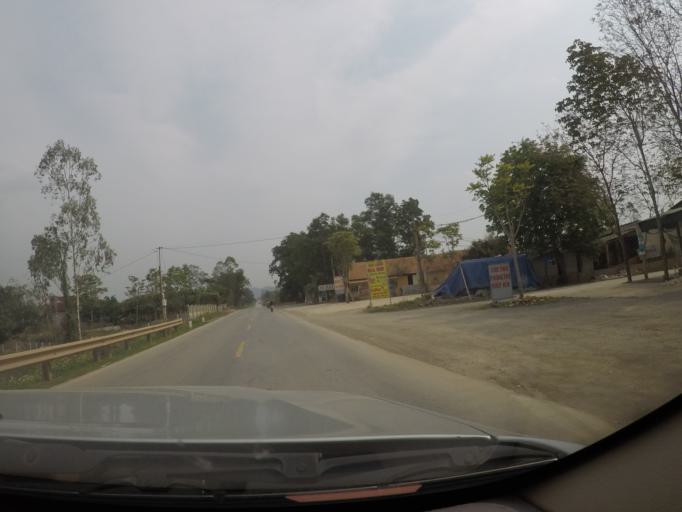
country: VN
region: Nghe An
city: Cau Giat
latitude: 19.3532
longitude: 105.4709
